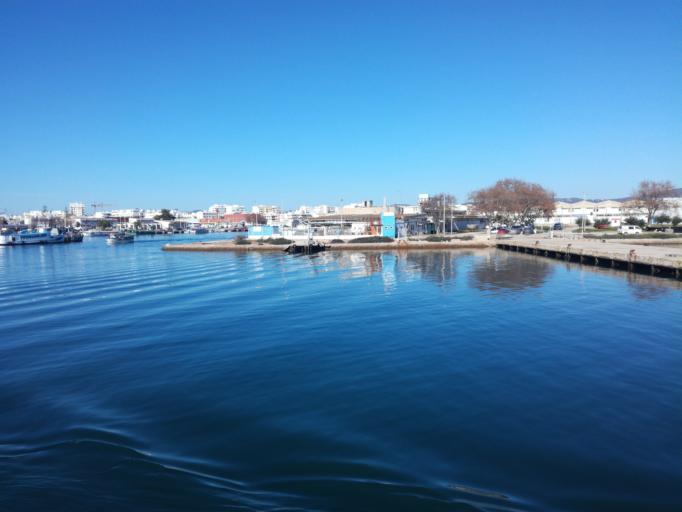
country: PT
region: Faro
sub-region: Olhao
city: Olhao
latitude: 37.0233
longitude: -7.8329
